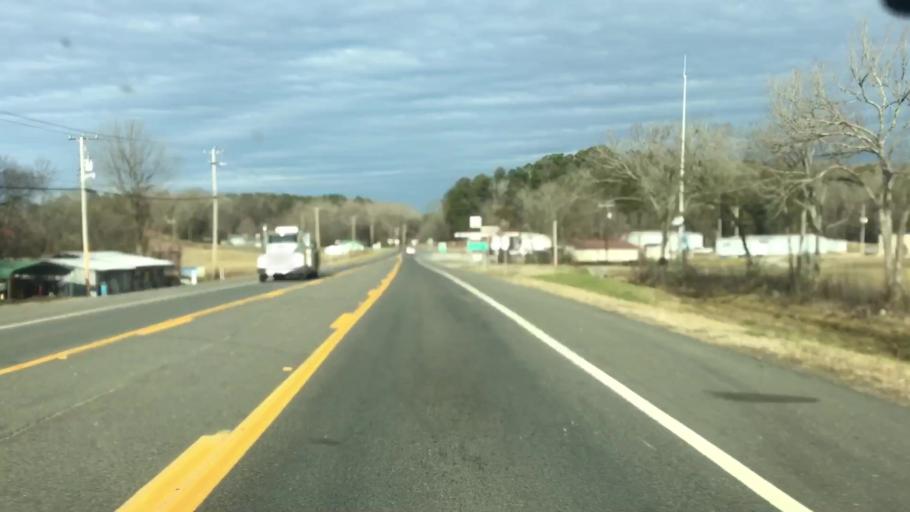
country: US
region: Arkansas
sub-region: Montgomery County
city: Mount Ida
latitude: 34.5610
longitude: -93.6373
